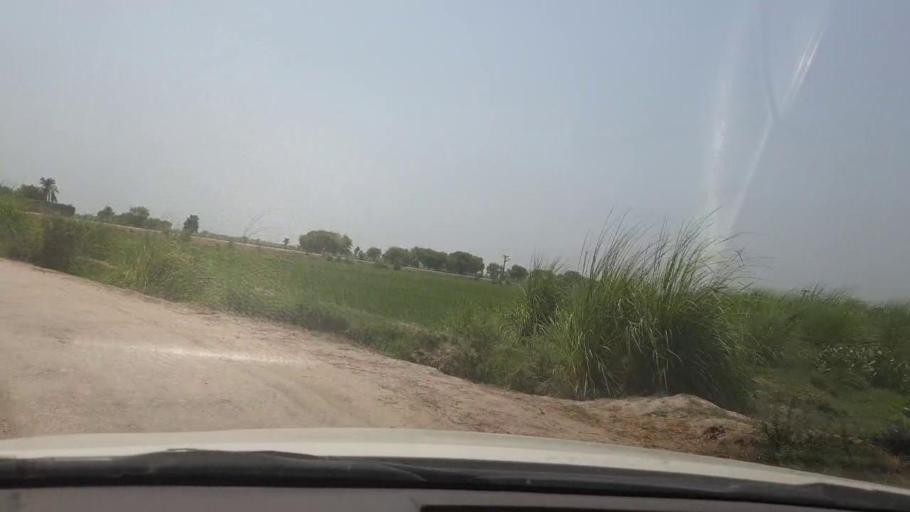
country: PK
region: Sindh
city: Shikarpur
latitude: 28.0710
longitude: 68.5366
